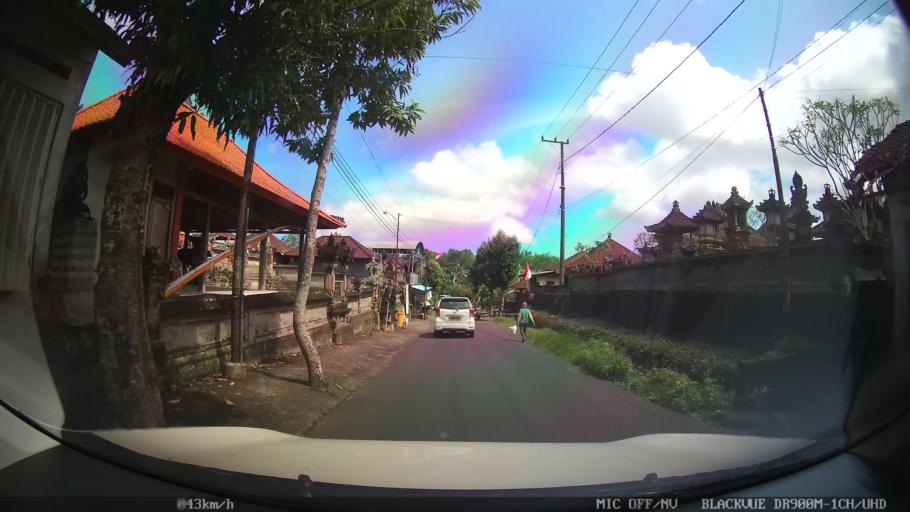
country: ID
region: Bali
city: Banjar Mulung
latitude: -8.5129
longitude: 115.3189
